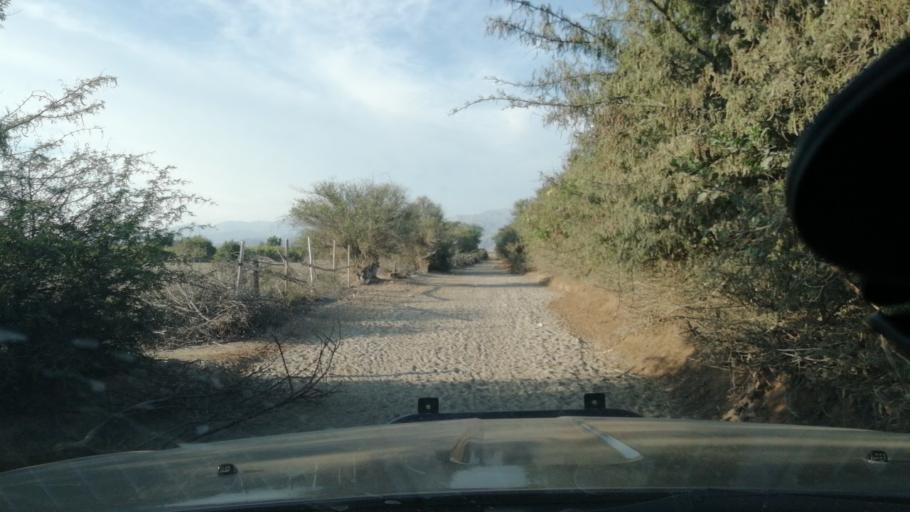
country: PE
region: Ica
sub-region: Provincia de Chincha
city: San Pedro
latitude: -13.3430
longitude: -76.1593
